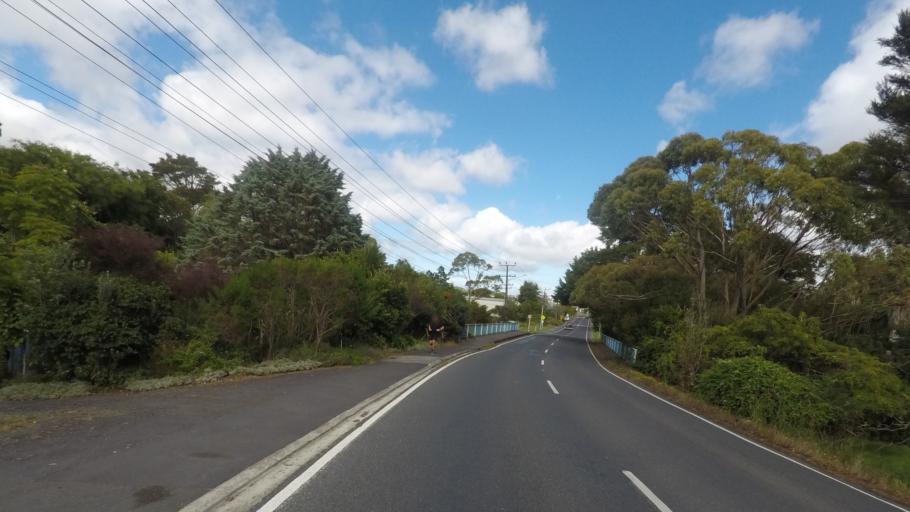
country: NZ
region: Auckland
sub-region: Auckland
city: Muriwai Beach
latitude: -36.7701
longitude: 174.5497
